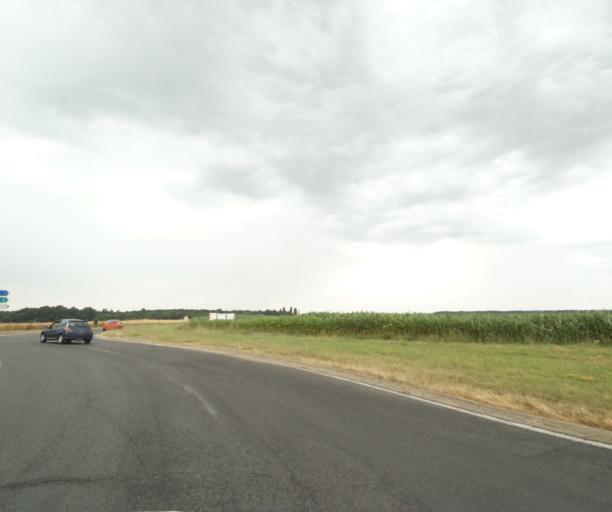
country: FR
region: Ile-de-France
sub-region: Departement de Seine-et-Marne
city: Pringy
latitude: 48.4942
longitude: 2.5838
